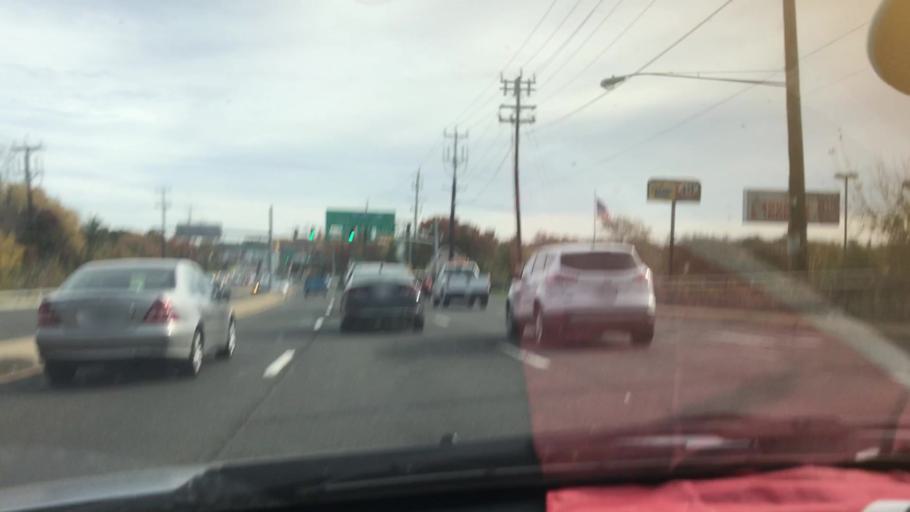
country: US
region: Maryland
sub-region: Prince George's County
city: Largo
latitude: 38.8908
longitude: -76.8517
